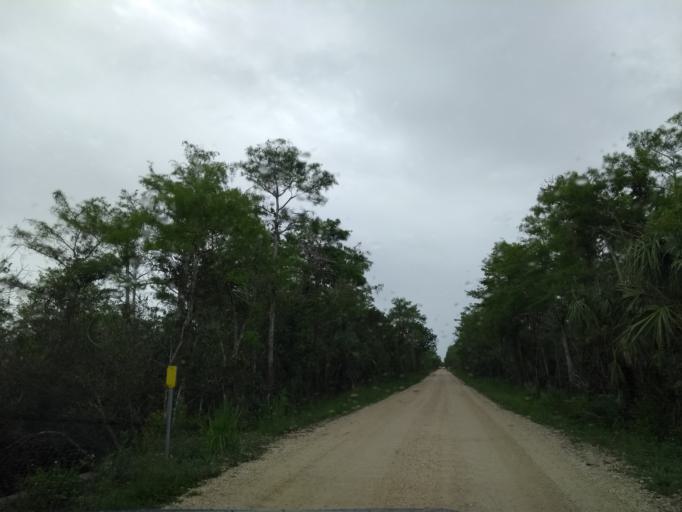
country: US
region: Florida
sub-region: Miami-Dade County
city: The Hammocks
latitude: 25.7576
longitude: -80.9877
